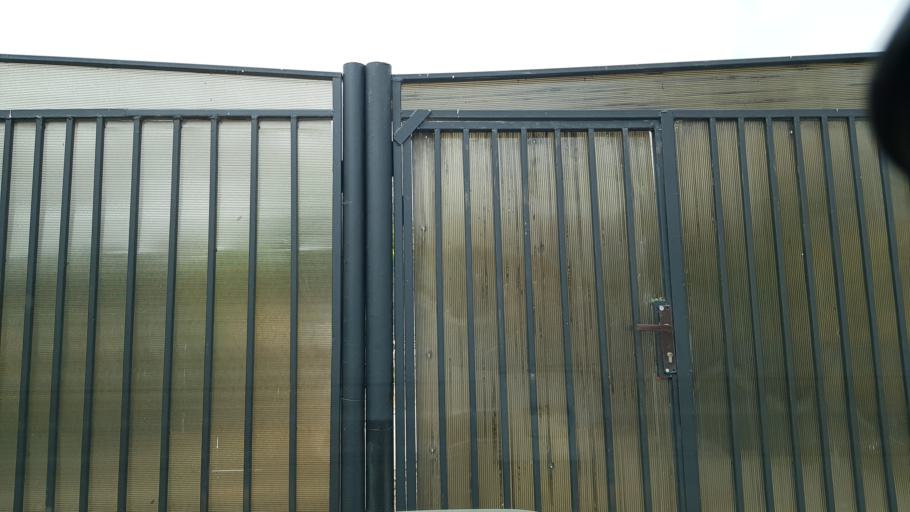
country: RO
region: Ilfov
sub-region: Comuna Ganeasa
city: Ganeasa
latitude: 44.4921
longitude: 26.2867
